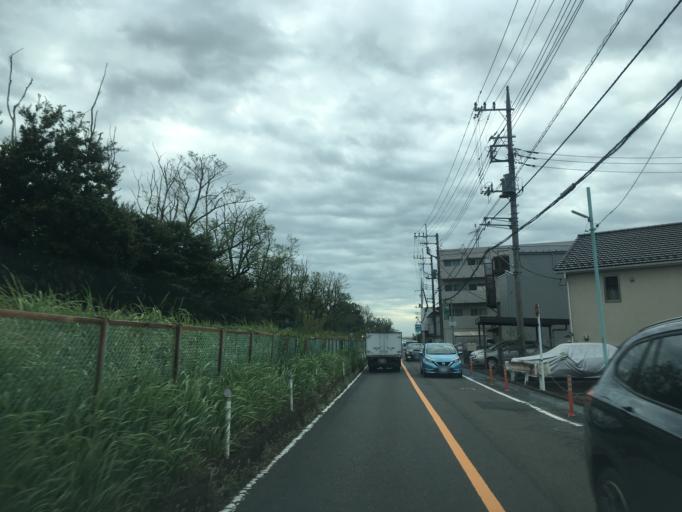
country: JP
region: Tokyo
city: Chofugaoka
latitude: 35.6486
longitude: 139.5162
